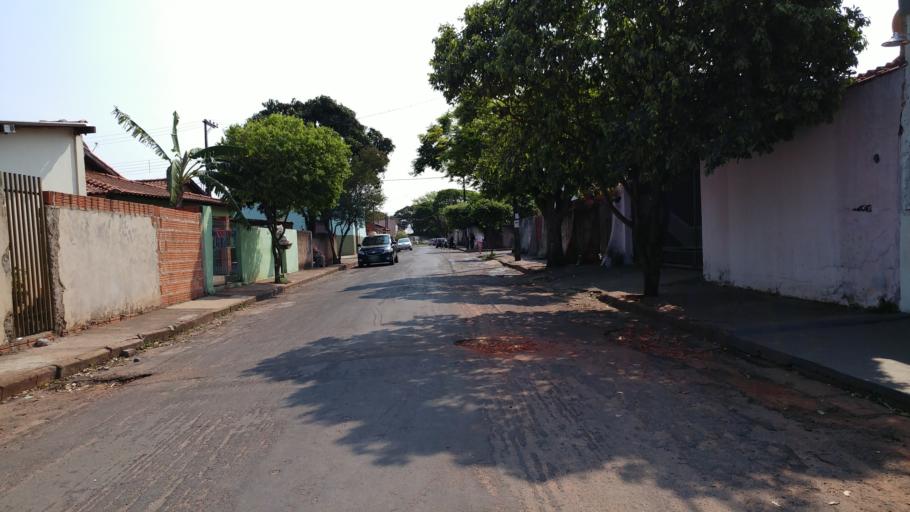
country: BR
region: Sao Paulo
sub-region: Paraguacu Paulista
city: Paraguacu Paulista
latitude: -22.4311
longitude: -50.5824
